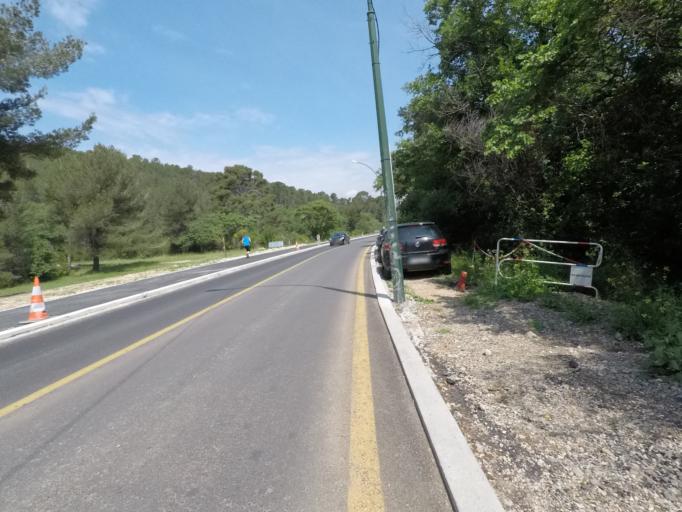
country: FR
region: Provence-Alpes-Cote d'Azur
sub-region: Departement des Bouches-du-Rhone
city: Marseille 09
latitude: 43.2331
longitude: 5.4360
